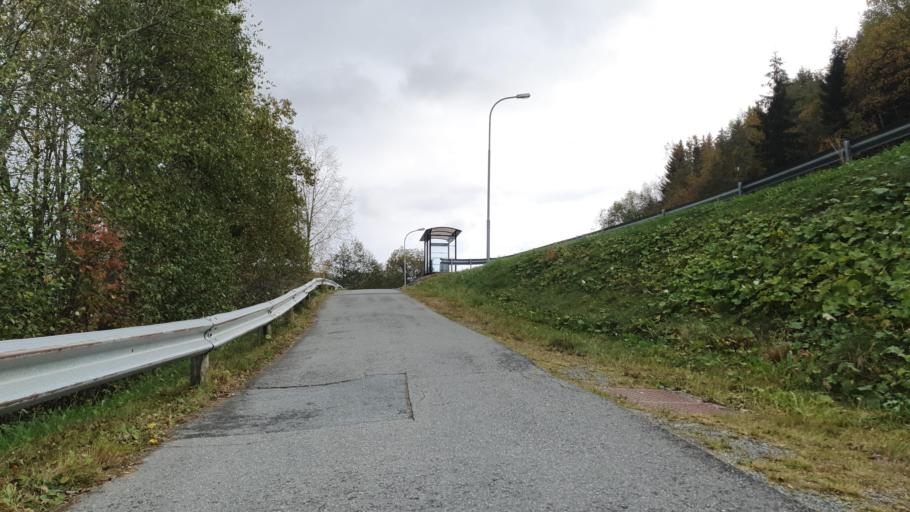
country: NO
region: Sor-Trondelag
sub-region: Klaebu
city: Klaebu
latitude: 63.3040
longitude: 10.4624
